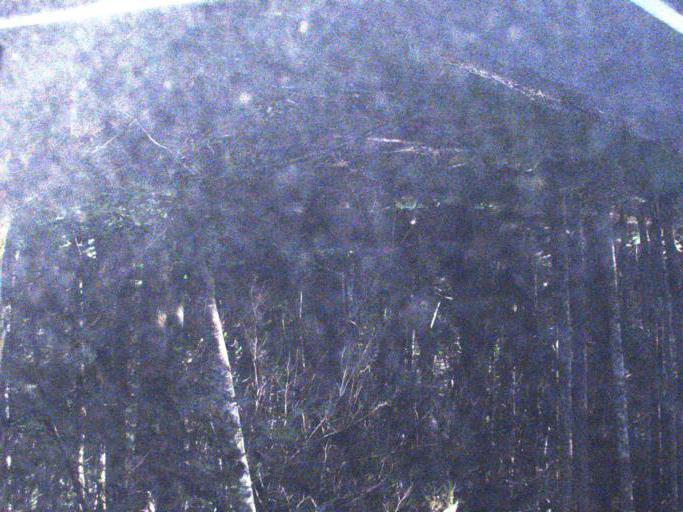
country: US
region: Washington
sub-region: King County
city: Riverbend
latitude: 47.1191
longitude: -121.6101
